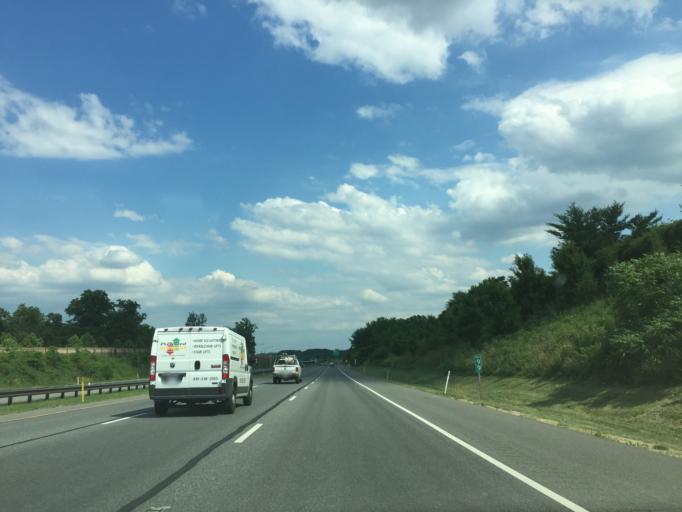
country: US
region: Maryland
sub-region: Montgomery County
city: Layhill
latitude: 39.1048
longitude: -77.0508
